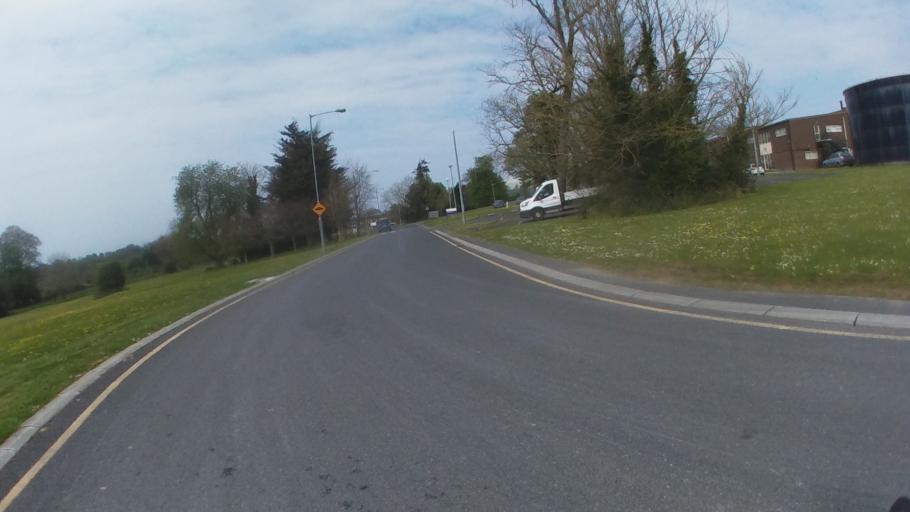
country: IE
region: Leinster
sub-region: Kilkenny
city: Kilkenny
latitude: 52.6433
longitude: -7.2109
